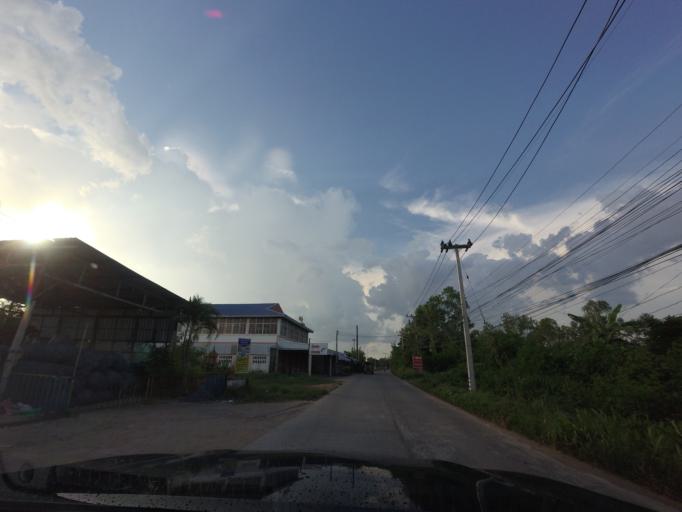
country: TH
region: Khon Kaen
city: Khon Kaen
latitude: 16.4025
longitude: 102.8654
